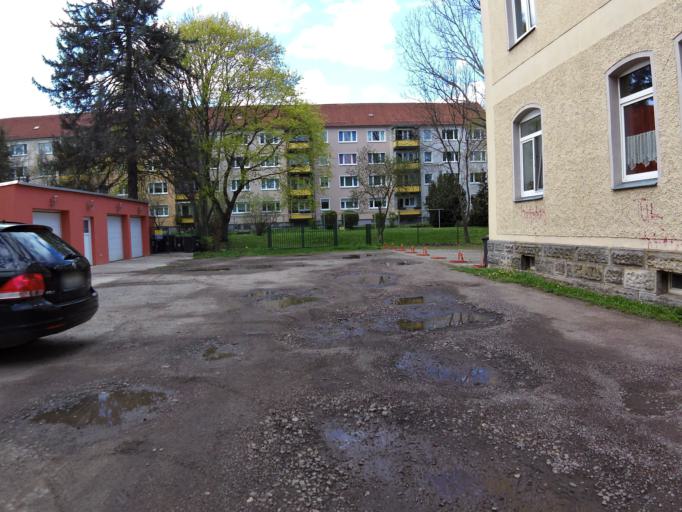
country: DE
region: Thuringia
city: Gotha
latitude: 50.9448
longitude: 10.6916
